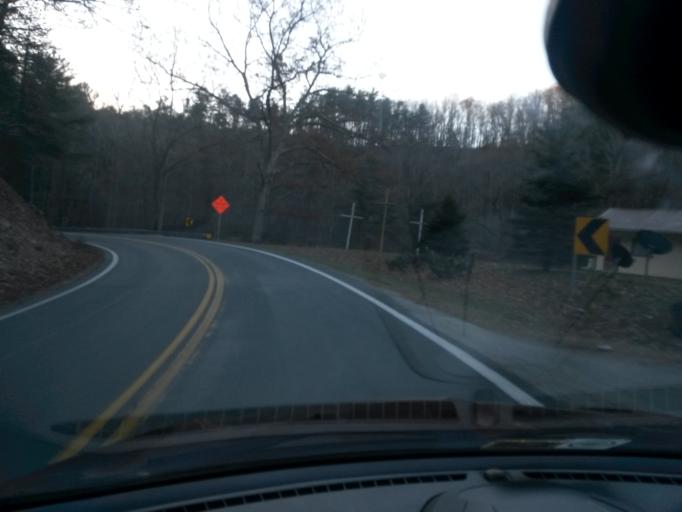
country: US
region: Virginia
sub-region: City of Buena Vista
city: Buena Vista
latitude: 37.7443
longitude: -79.2731
